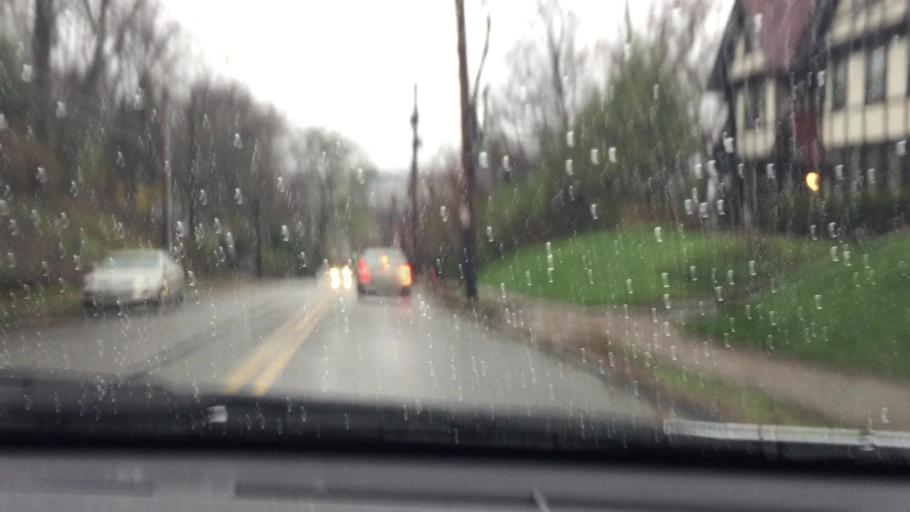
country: US
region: Pennsylvania
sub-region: Allegheny County
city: Bloomfield
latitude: 40.4471
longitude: -79.9346
